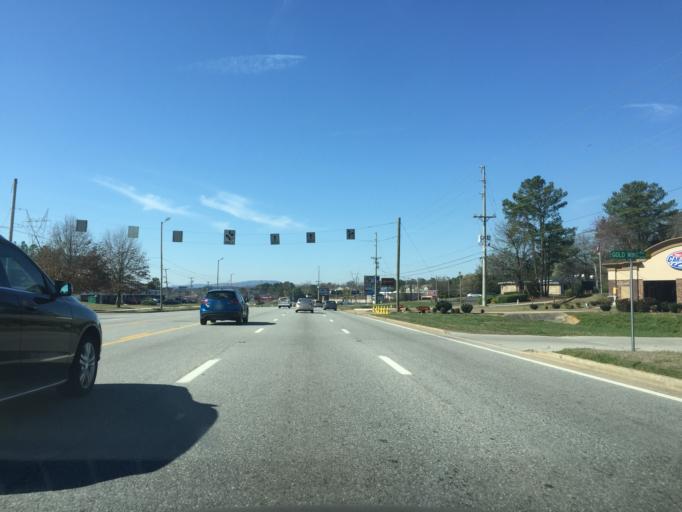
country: US
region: Tennessee
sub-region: Hamilton County
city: Harrison
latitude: 35.0925
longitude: -85.1819
